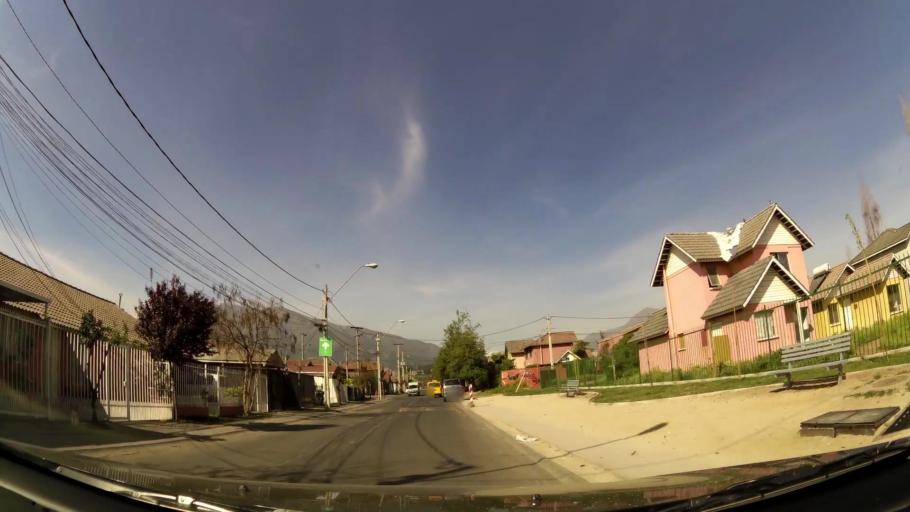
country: CL
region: Santiago Metropolitan
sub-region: Provincia de Cordillera
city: Puente Alto
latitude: -33.5883
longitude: -70.5562
